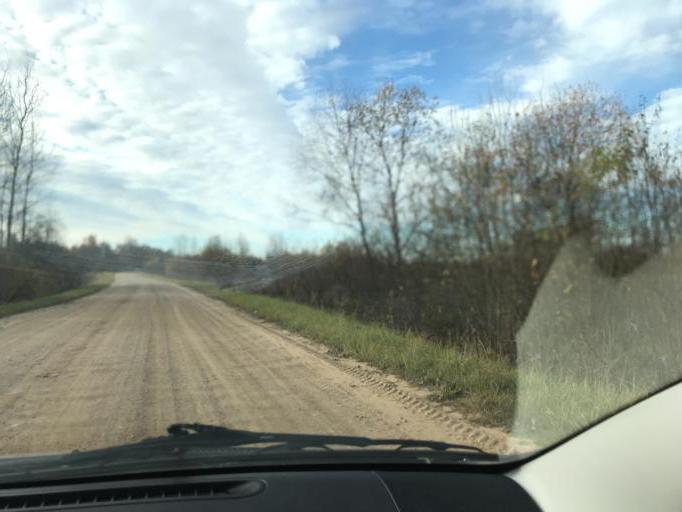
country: BY
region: Vitebsk
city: Haradok
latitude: 55.4568
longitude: 30.0426
